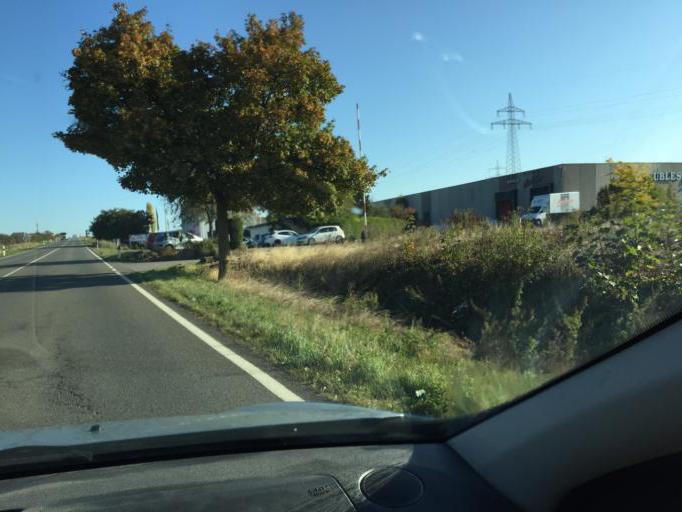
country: LU
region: Luxembourg
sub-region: Canton de Mersch
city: Bissen
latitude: 49.7810
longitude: 6.0896
